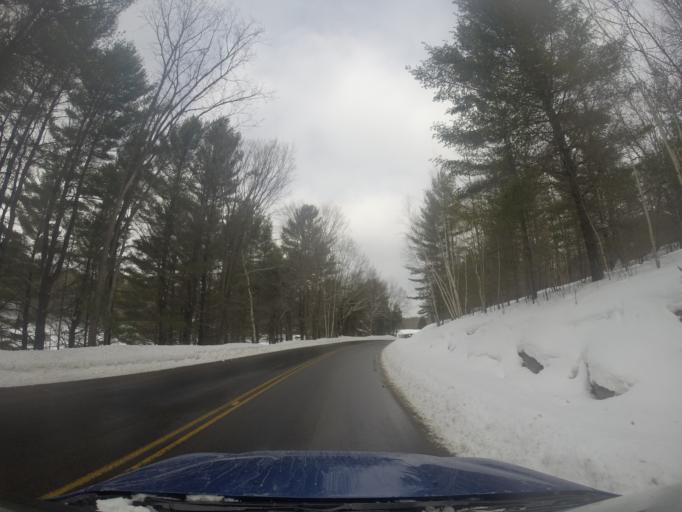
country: CA
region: Ontario
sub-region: Parry Sound District
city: Parry Sound
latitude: 45.3801
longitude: -80.0283
